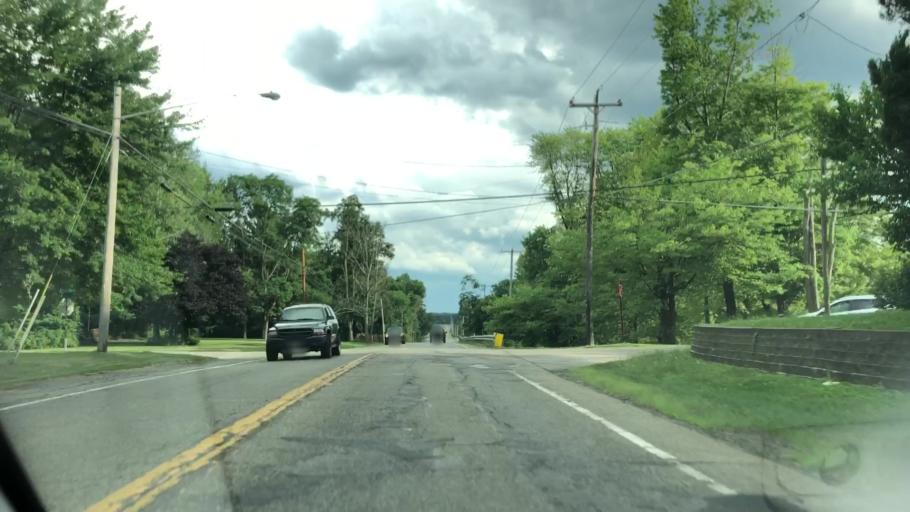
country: US
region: Ohio
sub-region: Summit County
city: Greensburg
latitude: 40.9214
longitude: -81.4630
